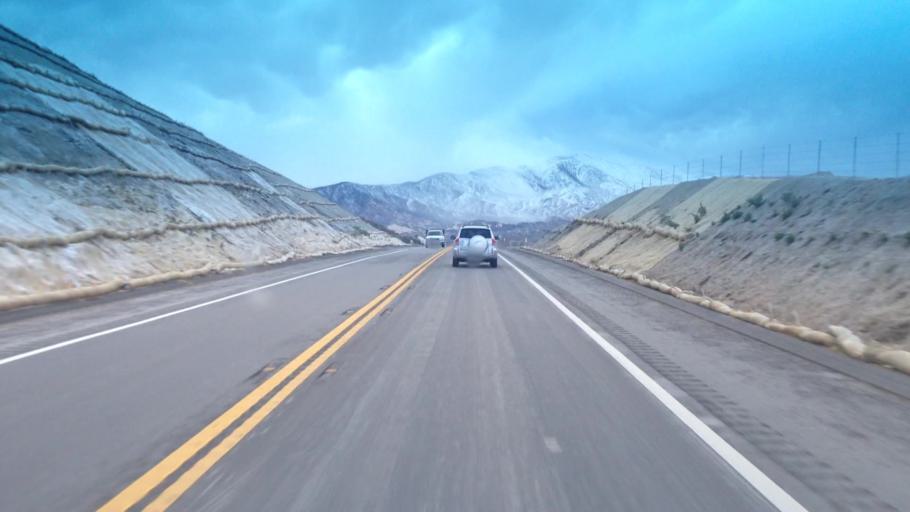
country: US
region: California
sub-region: San Bernardino County
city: Oak Hills
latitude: 34.3253
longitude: -117.4290
